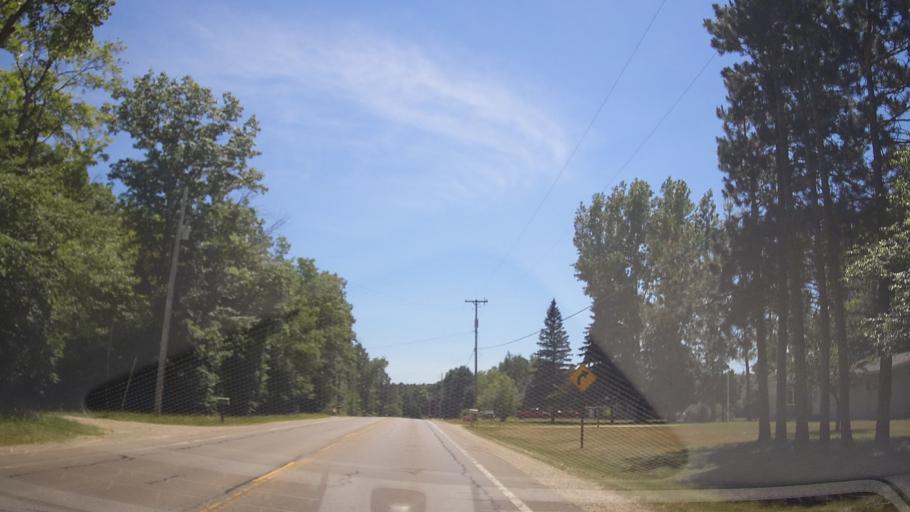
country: US
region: Michigan
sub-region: Grand Traverse County
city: Traverse City
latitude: 44.6893
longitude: -85.6901
